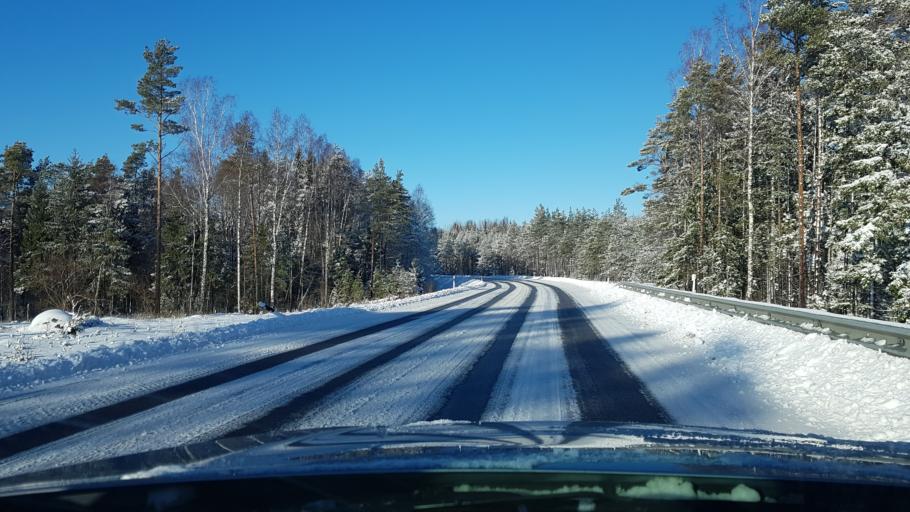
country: EE
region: Hiiumaa
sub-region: Kaerdla linn
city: Kardla
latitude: 58.9709
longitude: 22.7685
